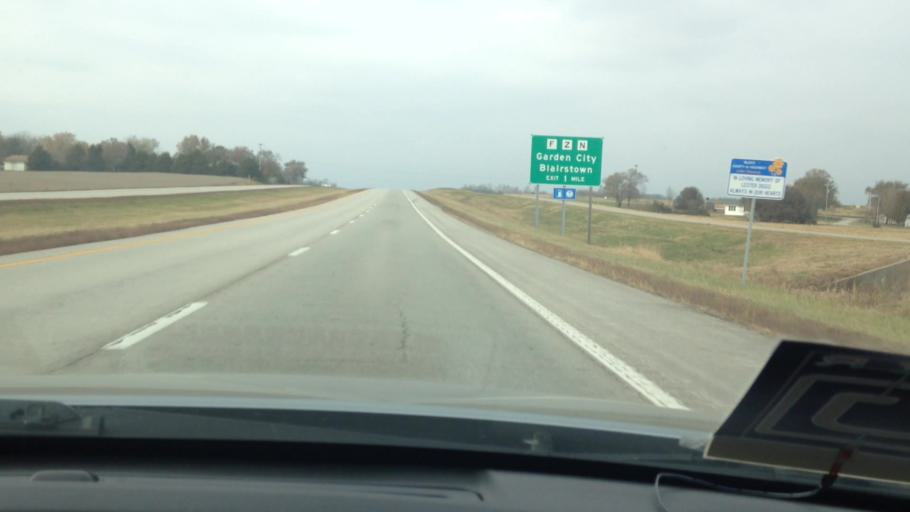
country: US
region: Missouri
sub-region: Cass County
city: Garden City
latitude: 38.5596
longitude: -94.1817
